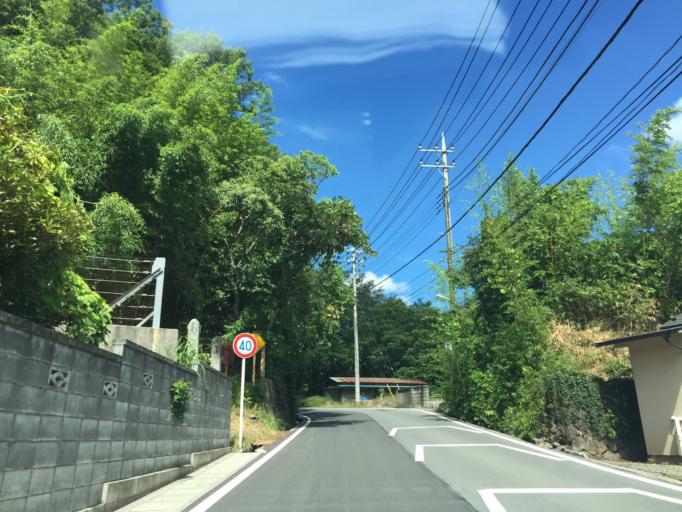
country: JP
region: Yamanashi
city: Nirasaki
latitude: 35.7887
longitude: 138.4058
